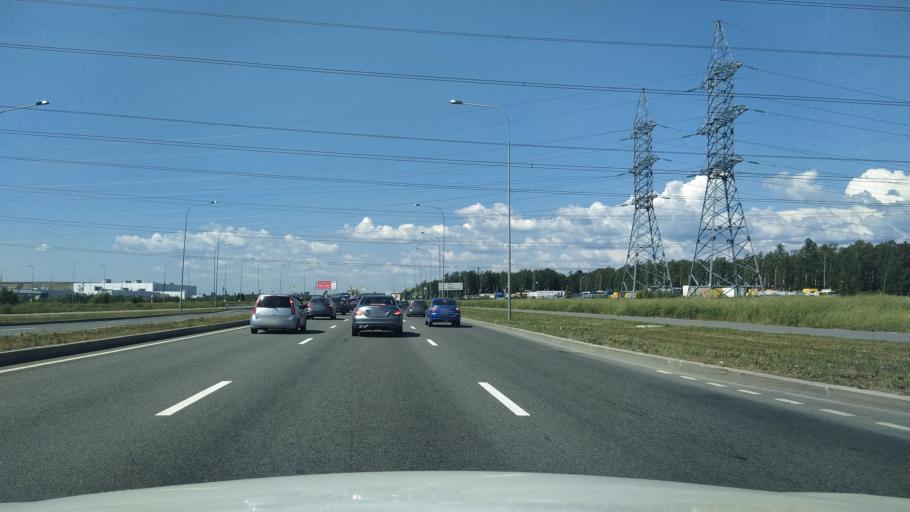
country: RU
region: St.-Petersburg
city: Levashovo
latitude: 60.0632
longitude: 30.1944
